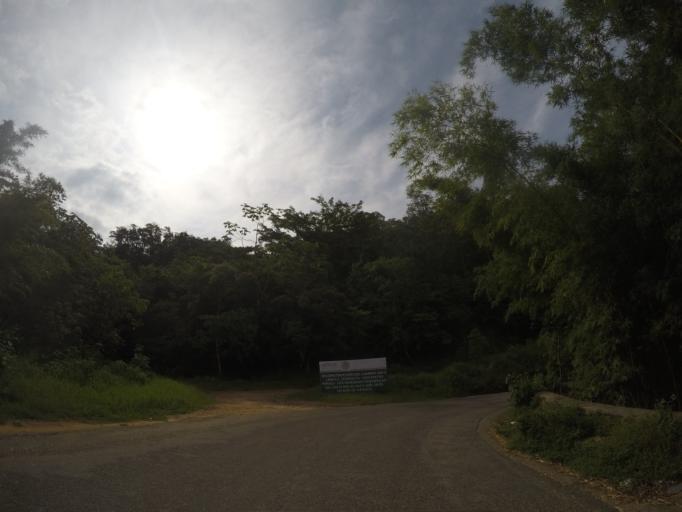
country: MX
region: Oaxaca
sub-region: San Pedro Pochutla
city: Los Naranjos Esquipulas
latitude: 15.9627
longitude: -96.4559
